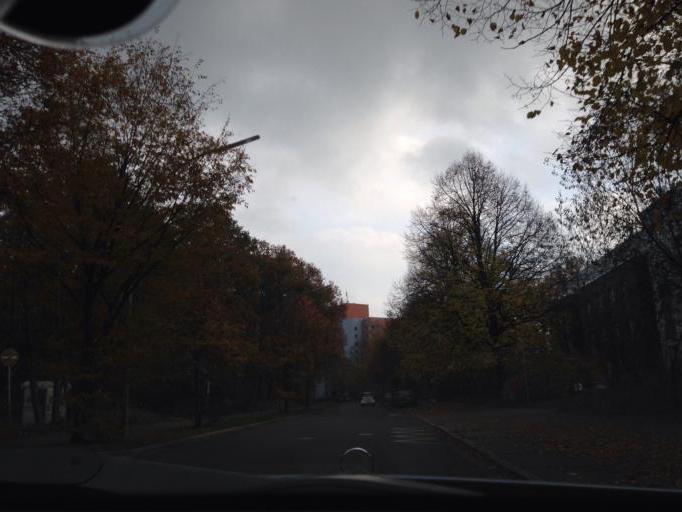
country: DE
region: Schleswig-Holstein
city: Barsbuettel
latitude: 53.5895
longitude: 10.1681
